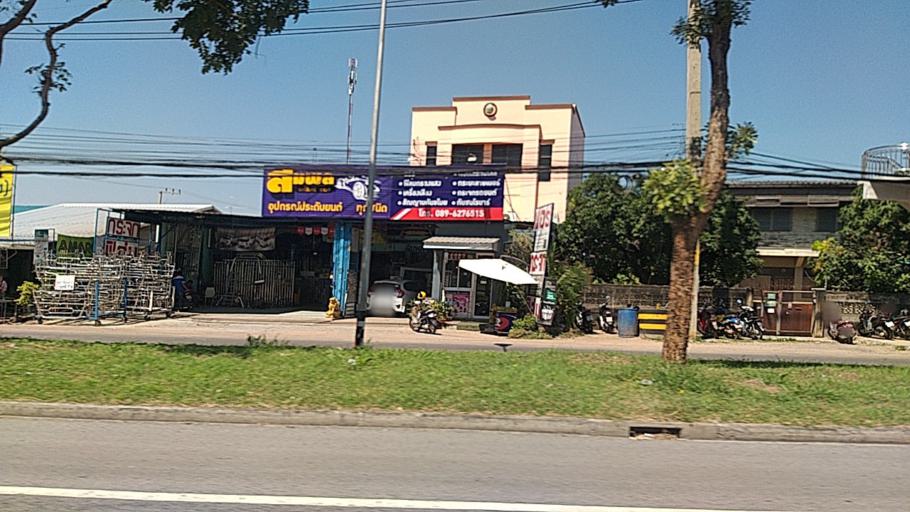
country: TH
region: Nakhon Ratchasima
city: Kham Thale So
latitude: 14.9265
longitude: 101.9650
